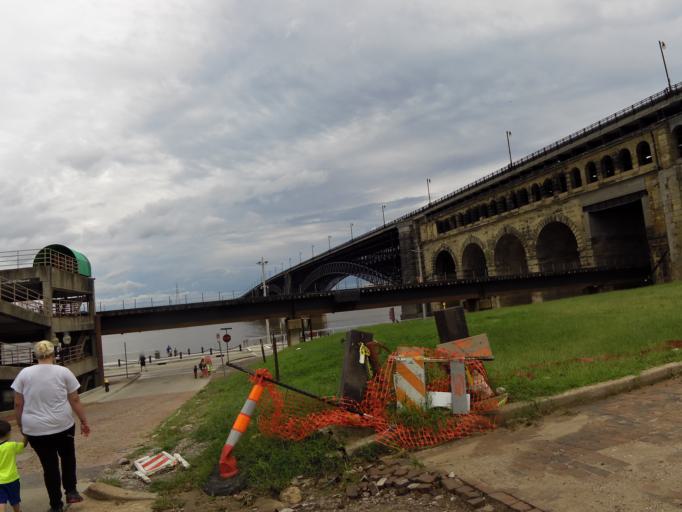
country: US
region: Missouri
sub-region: City of Saint Louis
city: St. Louis
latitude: 38.6298
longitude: -90.1829
